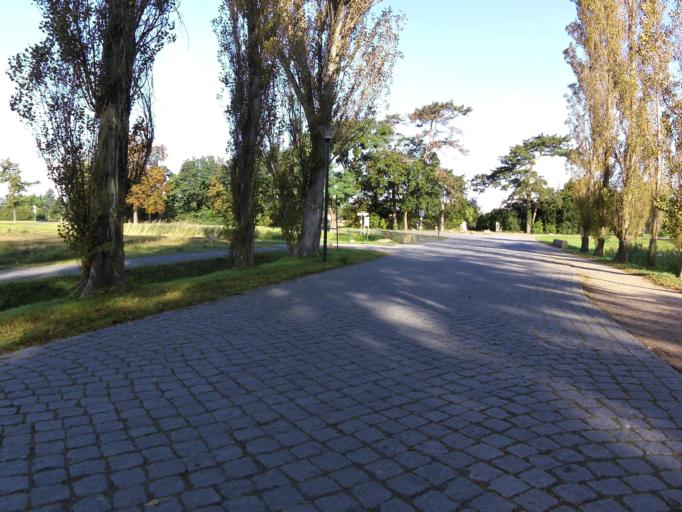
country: DE
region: Saxony-Anhalt
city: Worlitz
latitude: 51.8464
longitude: 12.4136
